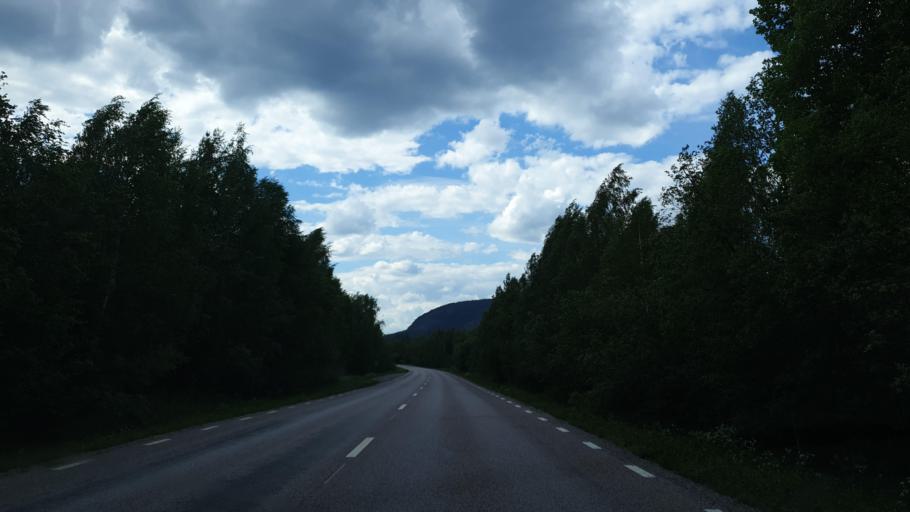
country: SE
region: Norrbotten
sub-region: Alvsbyns Kommun
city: AElvsbyn
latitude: 65.7812
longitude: 20.8158
